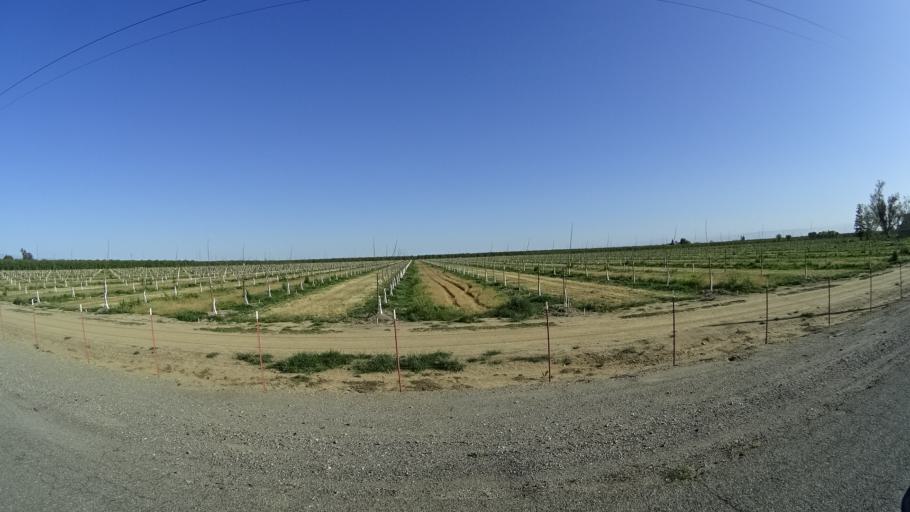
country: US
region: California
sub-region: Glenn County
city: Hamilton City
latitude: 39.6959
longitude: -122.0911
